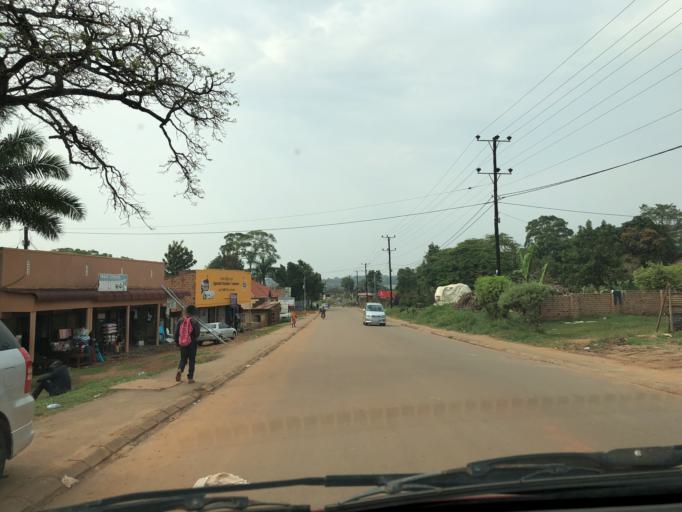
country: UG
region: Central Region
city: Kampala Central Division
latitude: 0.3967
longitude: 32.5932
